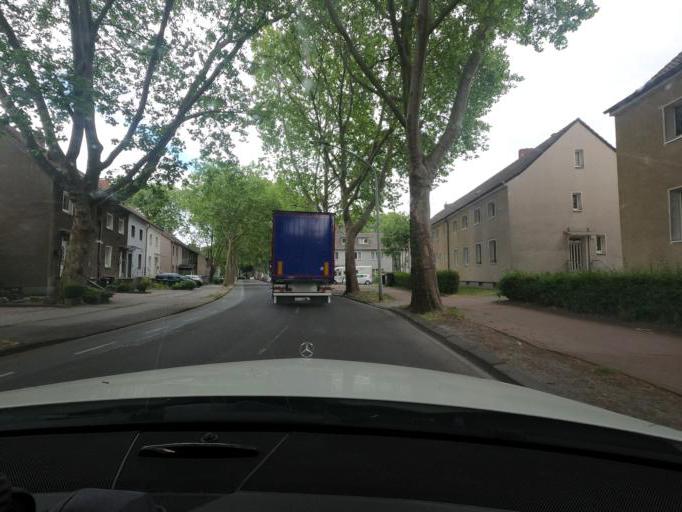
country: DE
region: North Rhine-Westphalia
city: Meiderich
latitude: 51.4799
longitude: 6.7458
